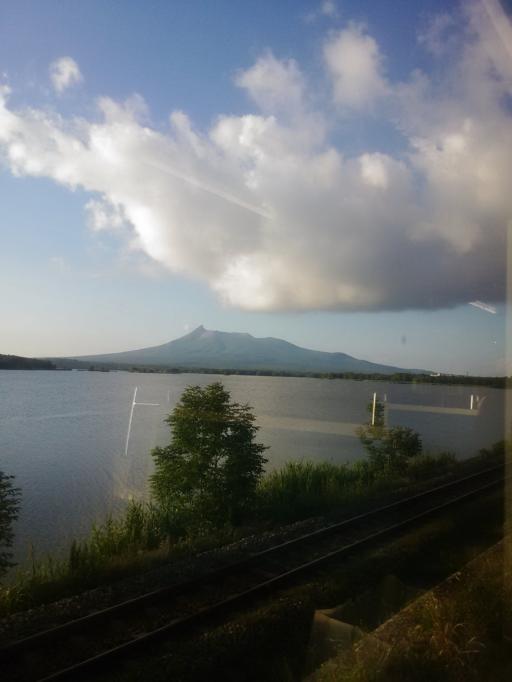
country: JP
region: Hokkaido
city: Nanae
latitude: 41.9571
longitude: 140.6547
